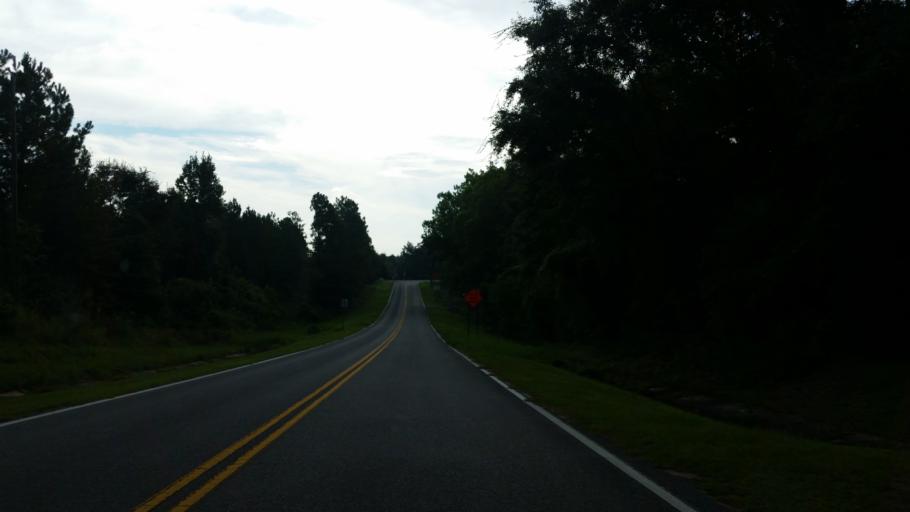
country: US
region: Florida
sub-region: Escambia County
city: Molino
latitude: 30.7739
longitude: -87.4815
